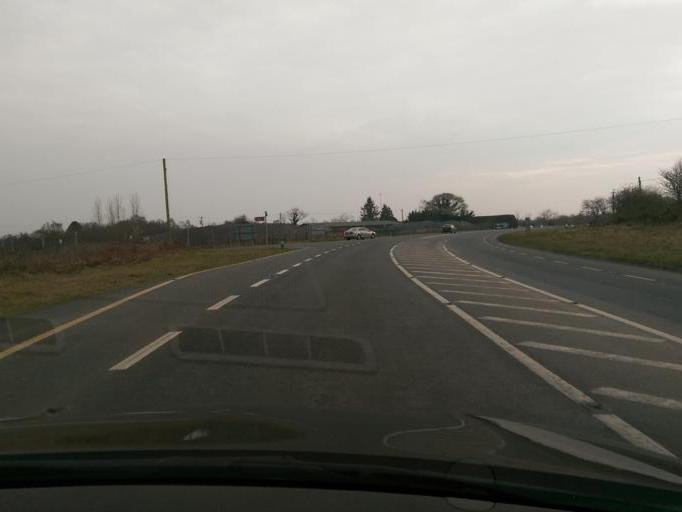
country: IE
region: Leinster
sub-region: An Iarmhi
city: Athlone
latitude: 53.4415
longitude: -7.8877
